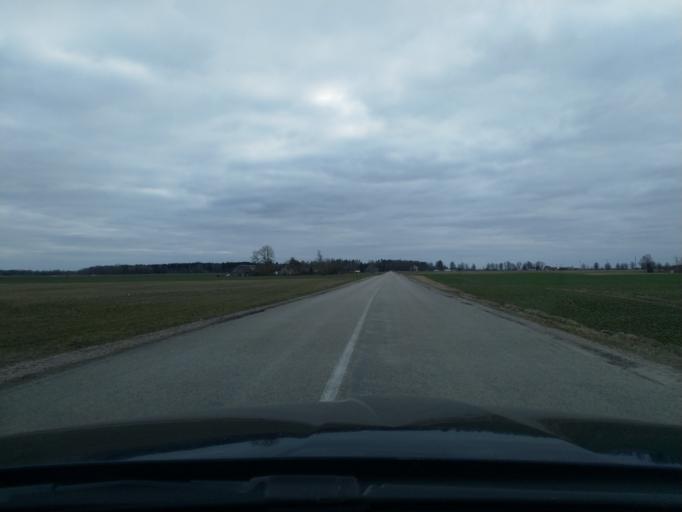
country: LV
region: Talsu Rajons
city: Sabile
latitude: 56.9430
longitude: 22.5998
